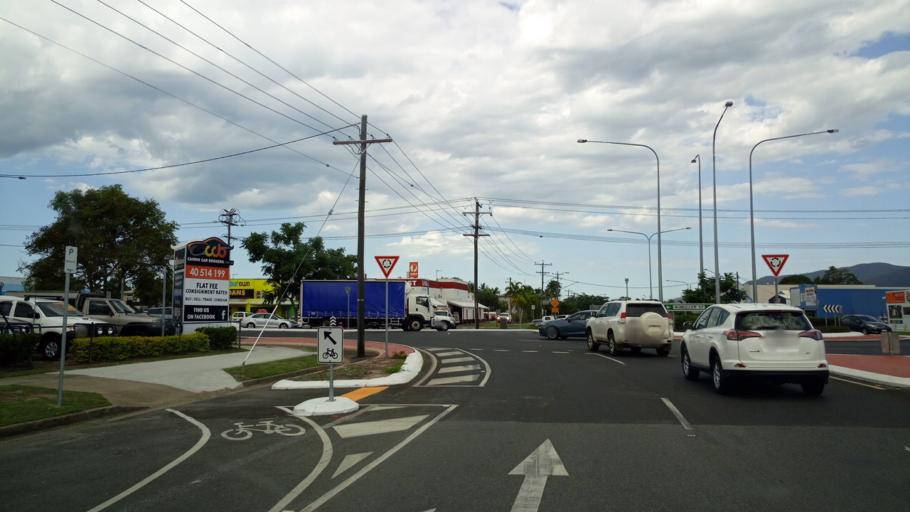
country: AU
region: Queensland
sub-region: Cairns
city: Cairns
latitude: -16.9336
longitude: 145.7606
